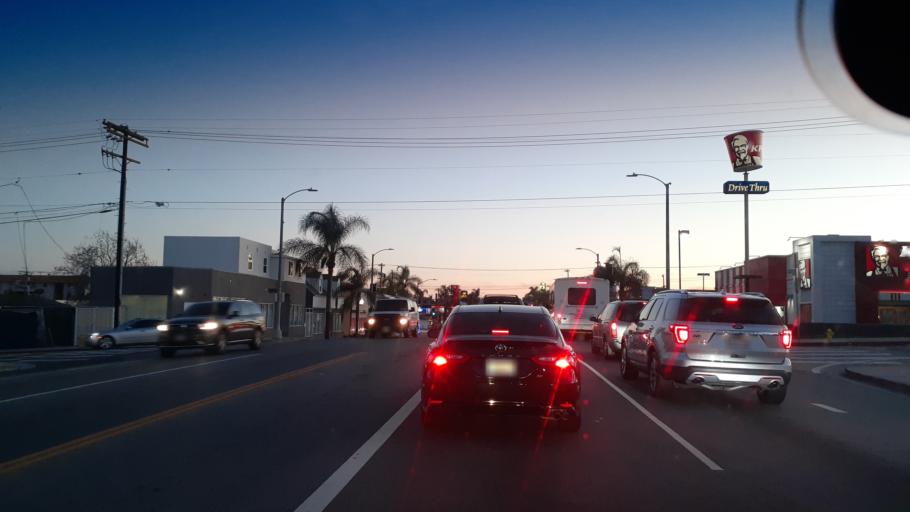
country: US
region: California
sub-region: Los Angeles County
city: San Pedro
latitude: 33.7409
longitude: -118.2924
